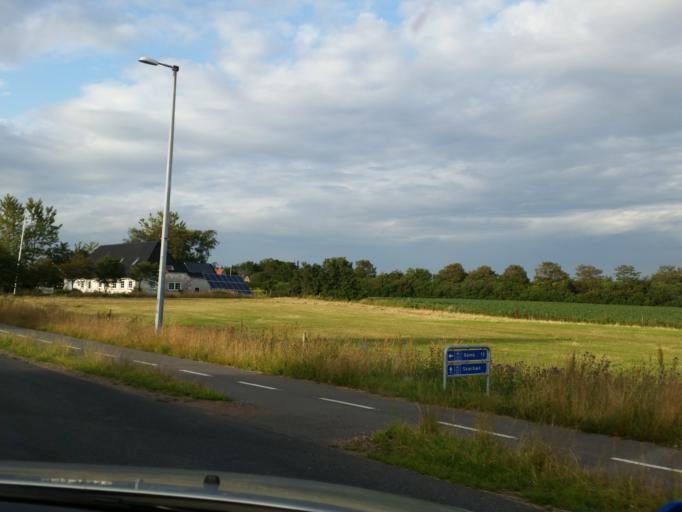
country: DK
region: South Denmark
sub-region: Tonder Kommune
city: Sherrebek
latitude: 55.1503
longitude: 8.7550
